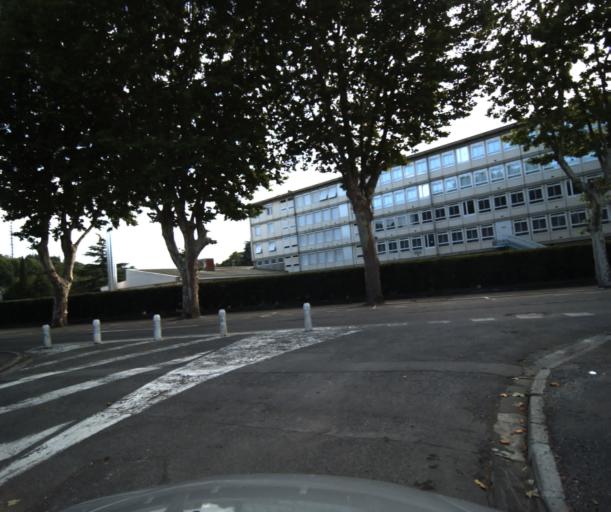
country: FR
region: Midi-Pyrenees
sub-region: Departement de la Haute-Garonne
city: Muret
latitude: 43.4541
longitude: 1.3325
